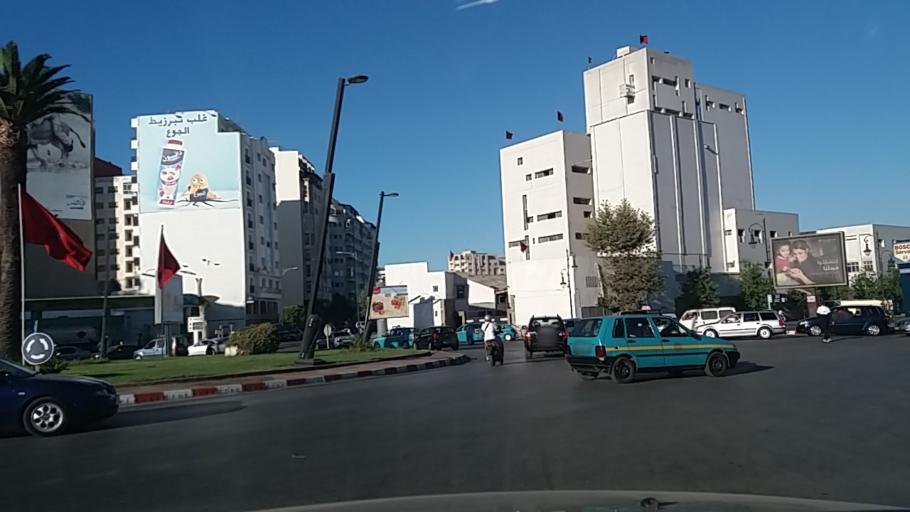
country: MA
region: Tanger-Tetouan
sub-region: Tanger-Assilah
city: Tangier
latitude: 35.7671
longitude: -5.8150
